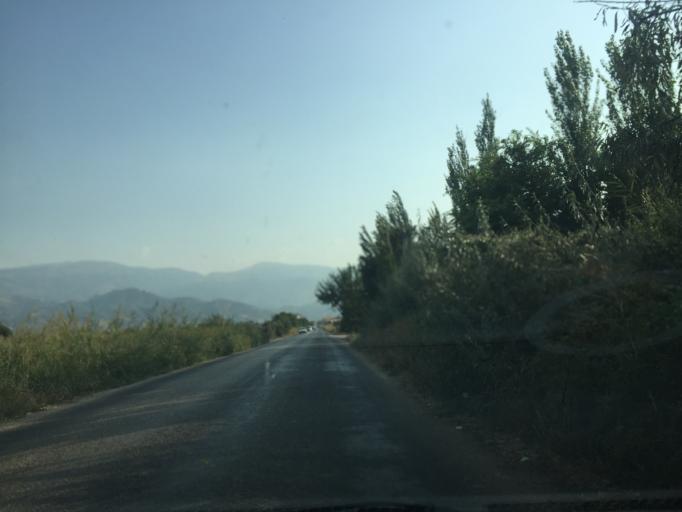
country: TR
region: Manisa
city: Salihli
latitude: 38.5024
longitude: 28.1861
